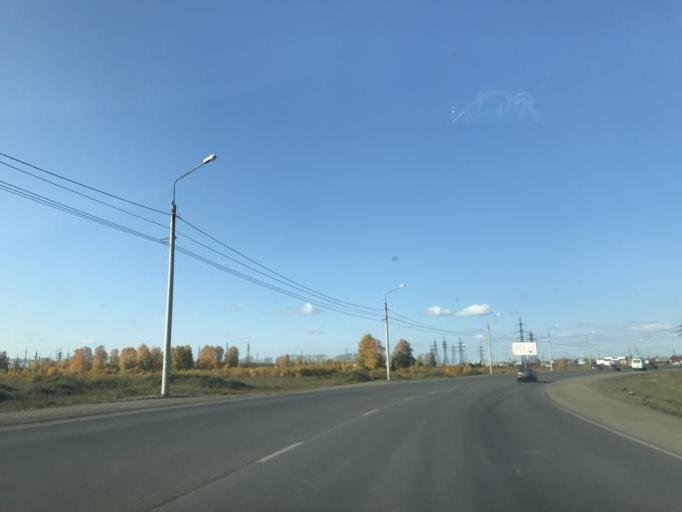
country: RU
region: Chelyabinsk
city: Roshchino
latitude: 55.2263
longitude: 61.2880
